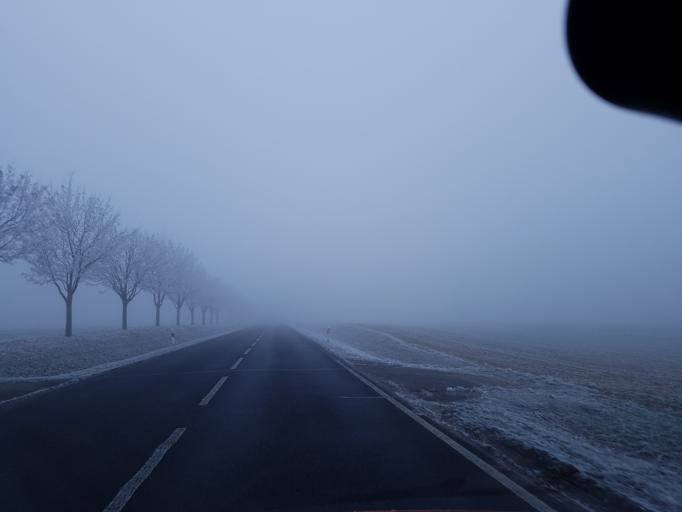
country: DE
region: Brandenburg
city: Muhlberg
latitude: 51.4581
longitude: 13.2423
